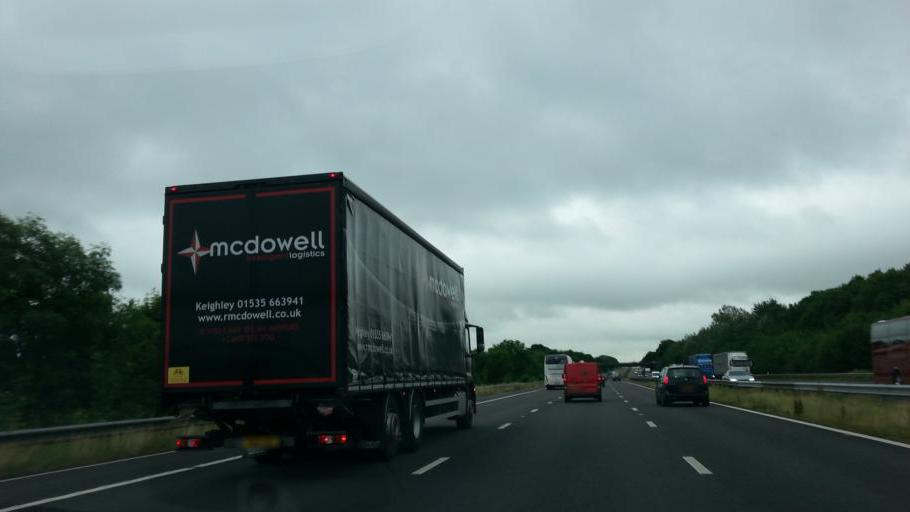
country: GB
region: England
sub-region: Leicestershire
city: Cosby
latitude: 52.5156
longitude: -1.1790
